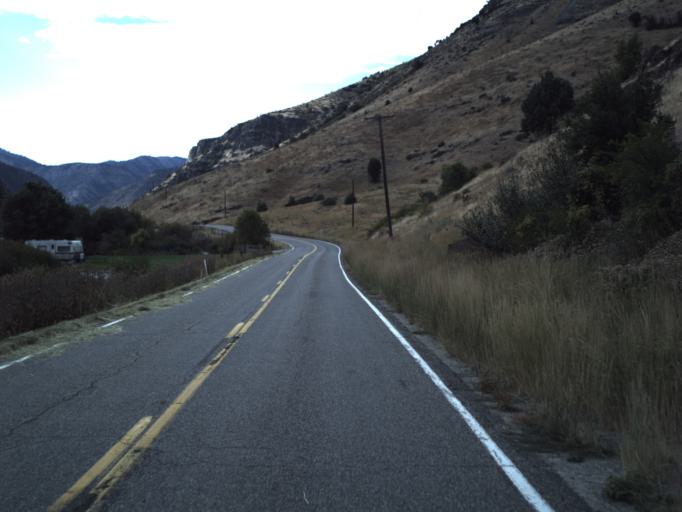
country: US
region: Utah
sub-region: Cache County
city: Millville
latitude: 41.6151
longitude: -111.6372
